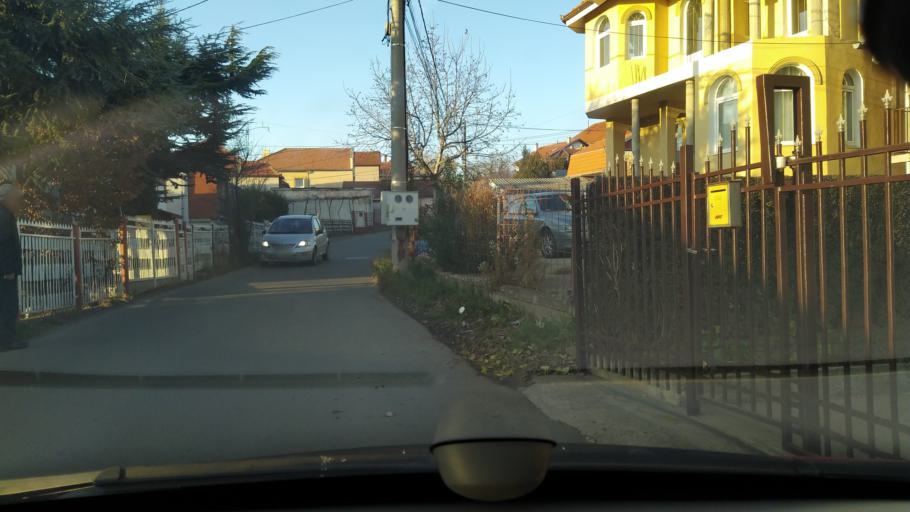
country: RS
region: Central Serbia
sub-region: Belgrade
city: Zvezdara
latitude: 44.7640
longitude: 20.5618
